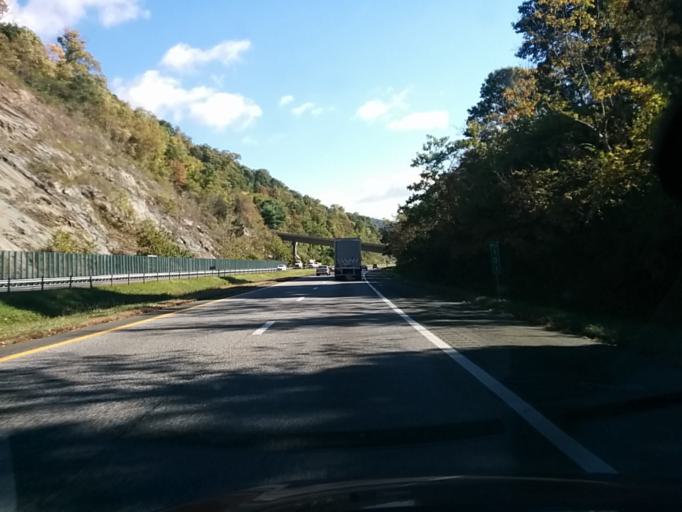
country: US
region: Virginia
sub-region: City of Waynesboro
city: Waynesboro
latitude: 38.0376
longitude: -78.8405
